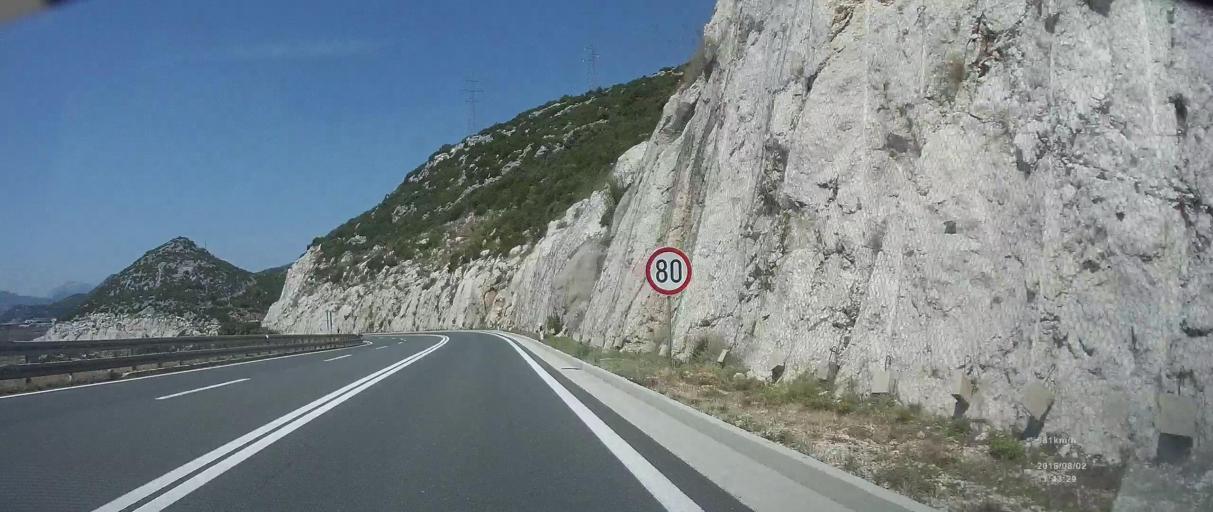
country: HR
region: Dubrovacko-Neretvanska
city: Komin
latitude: 43.0545
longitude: 17.4705
